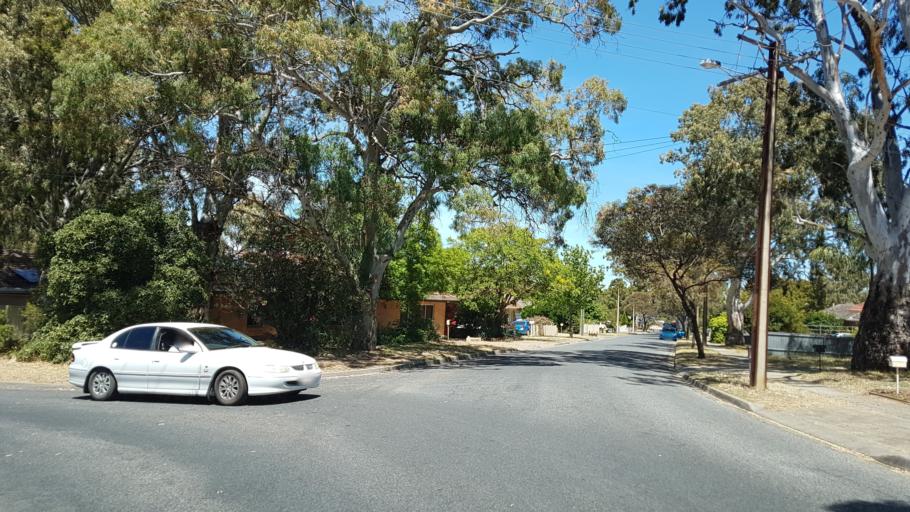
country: AU
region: South Australia
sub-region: Tea Tree Gully
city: Hope Valley
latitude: -34.8238
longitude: 138.7148
